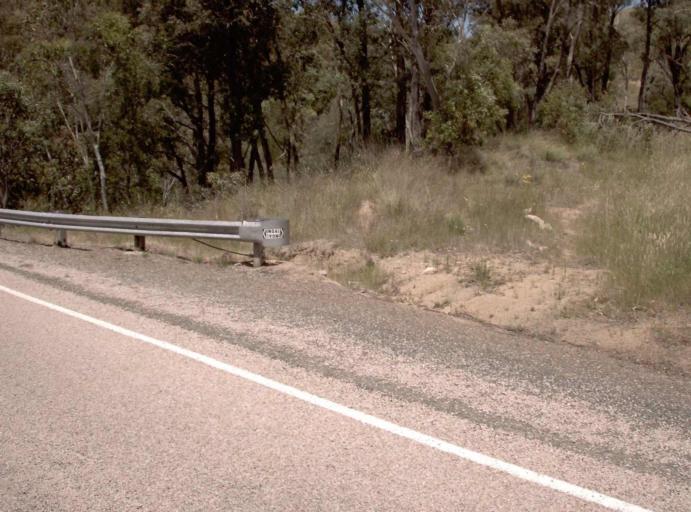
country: AU
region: Victoria
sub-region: Alpine
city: Mount Beauty
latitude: -37.1568
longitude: 147.6517
